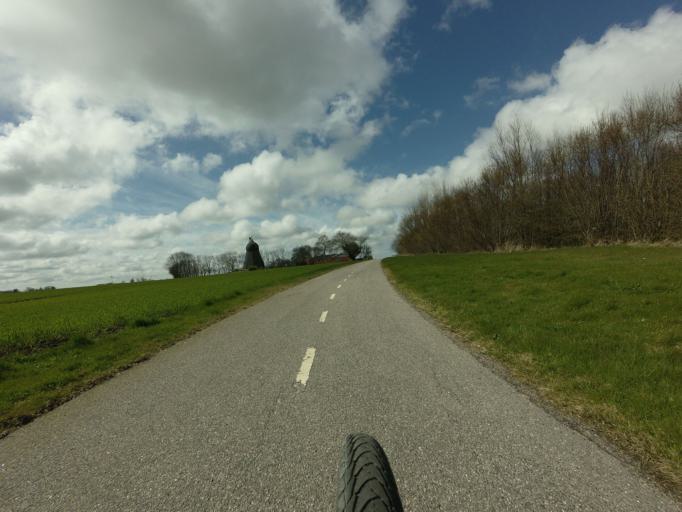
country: DK
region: North Denmark
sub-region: Hjorring Kommune
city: Vra
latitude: 57.3524
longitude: 9.9108
